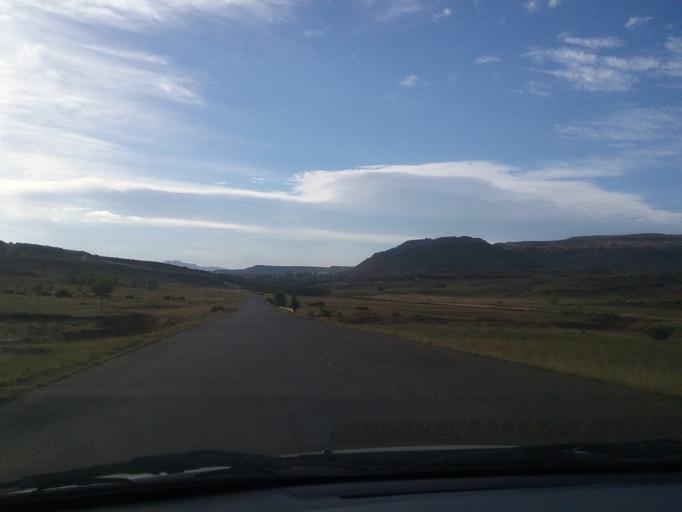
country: LS
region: Quthing
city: Quthing
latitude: -30.3855
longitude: 27.5983
